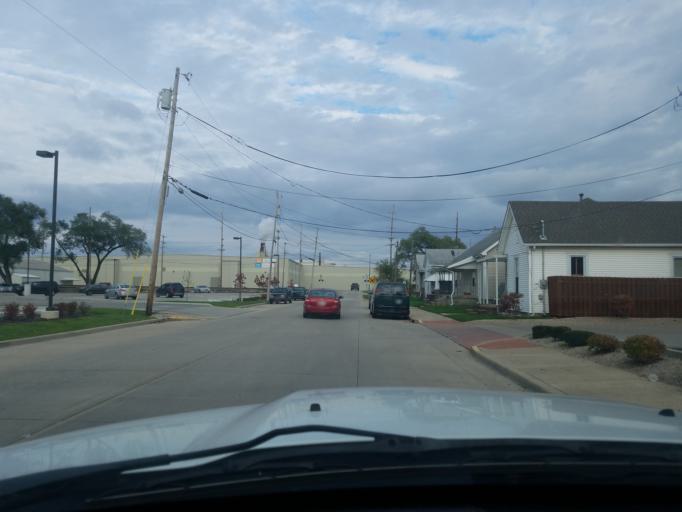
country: US
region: Indiana
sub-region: Shelby County
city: Shelbyville
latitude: 39.5280
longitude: -85.7768
